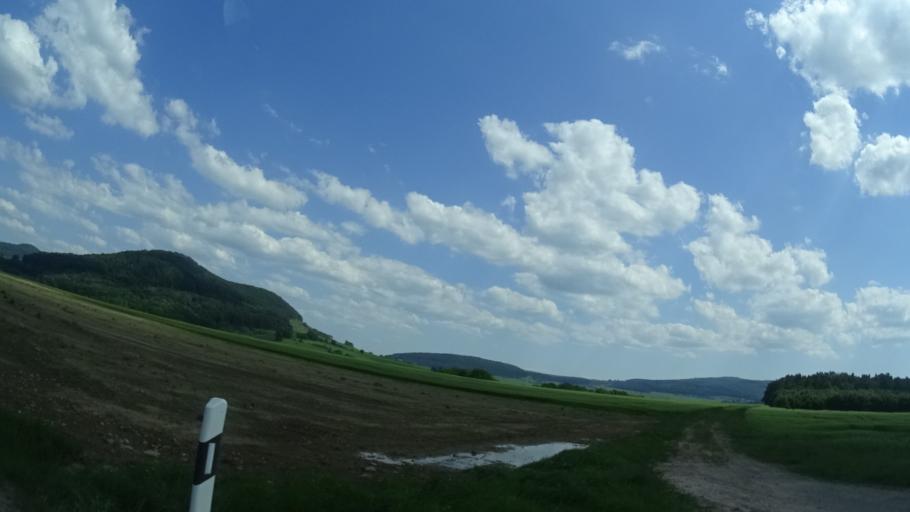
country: DE
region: Thuringia
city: Dermbach
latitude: 50.7247
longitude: 10.1550
